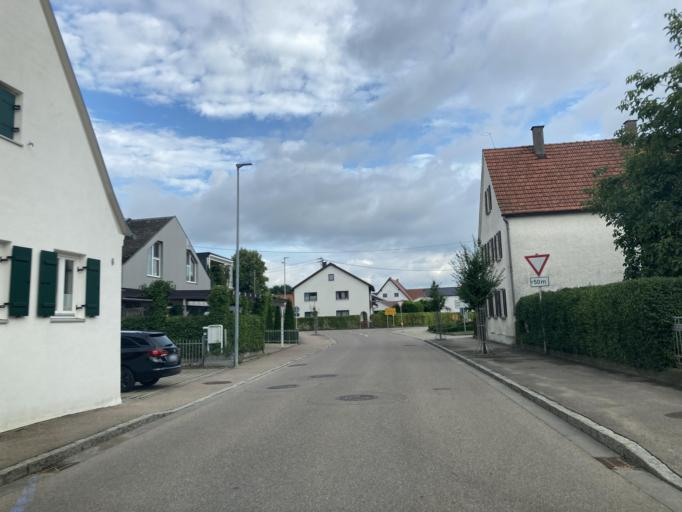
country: DE
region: Bavaria
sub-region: Swabia
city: Medlingen
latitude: 48.5681
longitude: 10.3176
